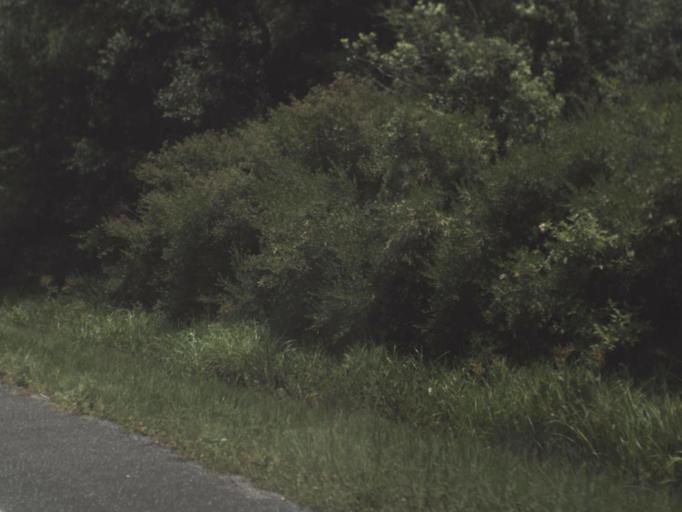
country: US
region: Florida
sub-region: Taylor County
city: Steinhatchee
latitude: 29.8577
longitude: -83.3089
